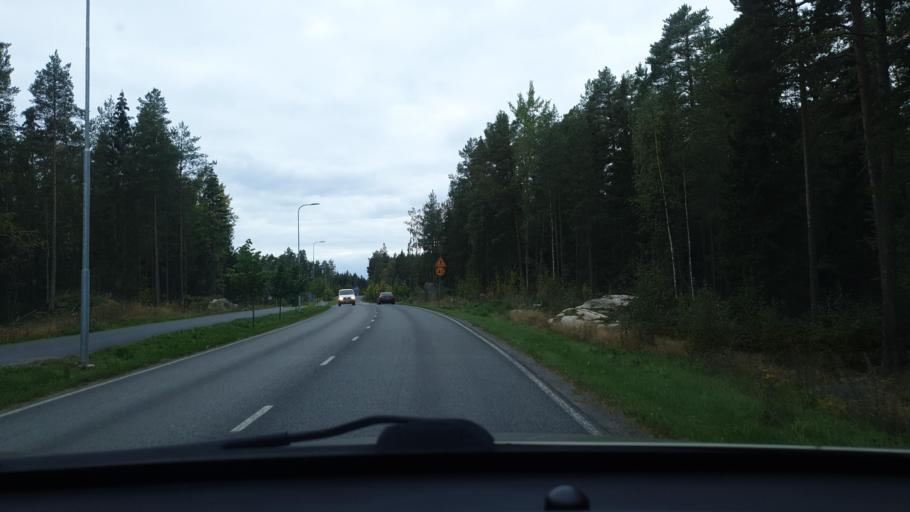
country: FI
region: Ostrobothnia
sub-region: Vaasa
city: Korsholm
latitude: 63.1206
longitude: 21.6473
